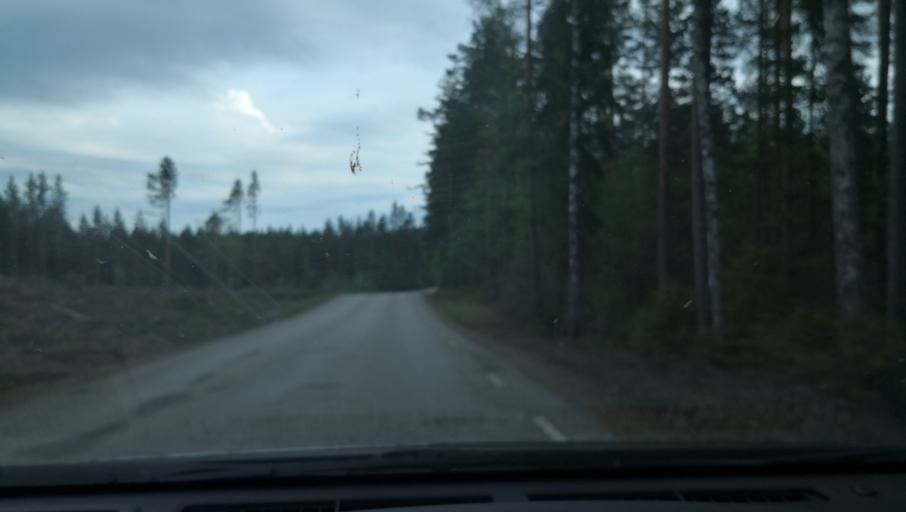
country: SE
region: Vaestmanland
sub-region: Skinnskattebergs Kommun
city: Skinnskatteberg
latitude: 59.8151
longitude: 15.5555
